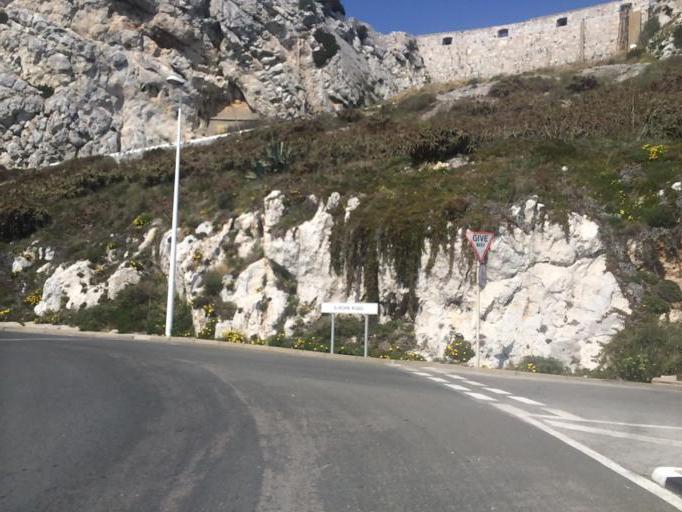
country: GI
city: Gibraltar
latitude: 36.1123
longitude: -5.3451
